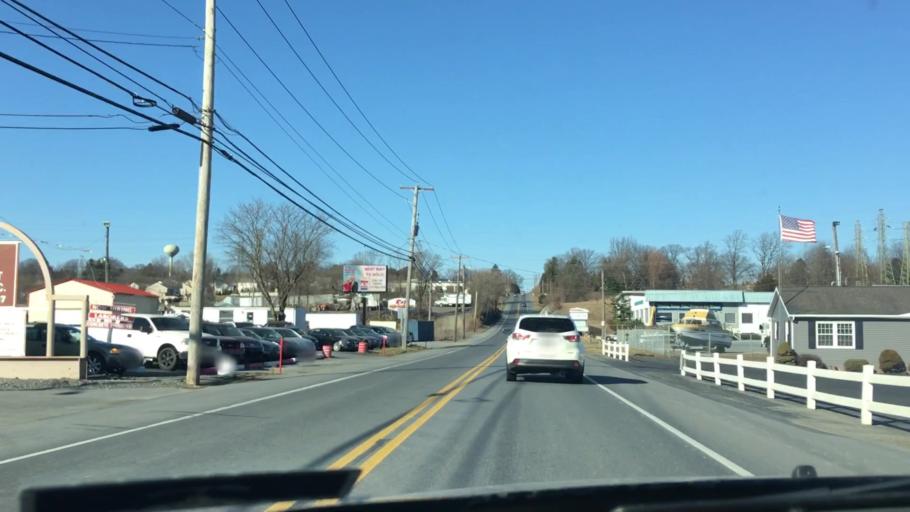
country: US
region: Pennsylvania
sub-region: Lancaster County
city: Brownstown
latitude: 40.1408
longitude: -76.2107
